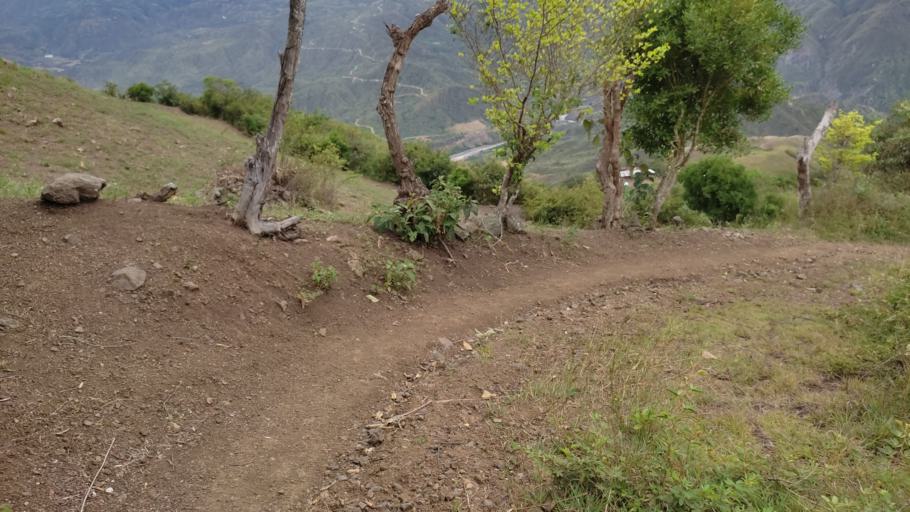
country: CO
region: Narino
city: Taminango
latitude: 1.5428
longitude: -77.3681
